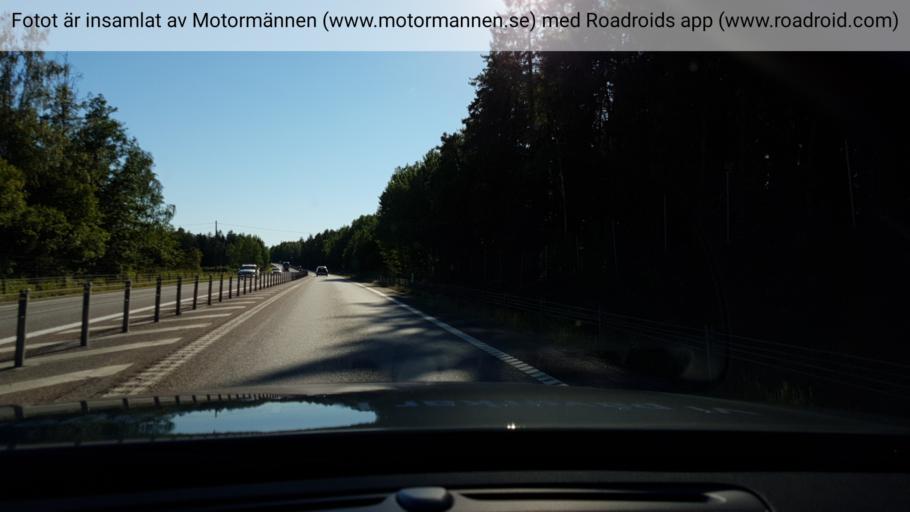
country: SE
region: Vaestmanland
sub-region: Hallstahammars Kommun
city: Hallstahammar
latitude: 59.5837
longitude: 16.1691
